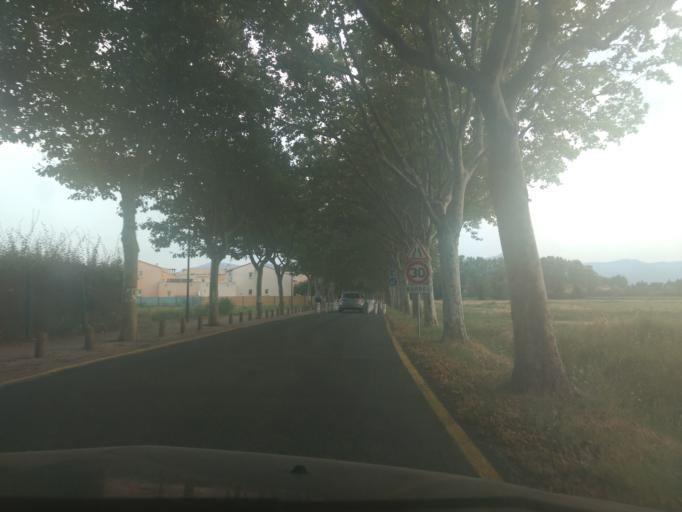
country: FR
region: Languedoc-Roussillon
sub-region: Departement des Pyrenees-Orientales
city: Latour-Bas-Elne
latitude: 42.6001
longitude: 3.0326
